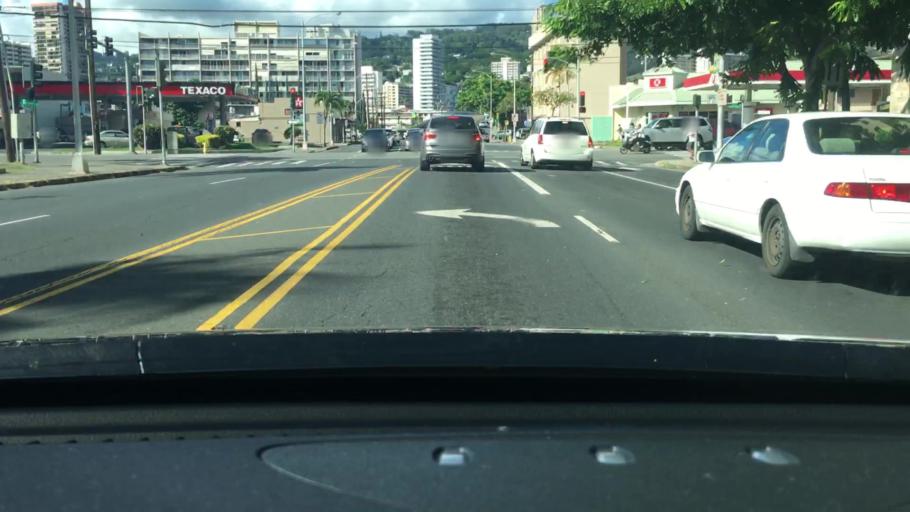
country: US
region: Hawaii
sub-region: Honolulu County
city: Honolulu
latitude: 21.2998
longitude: -157.8397
